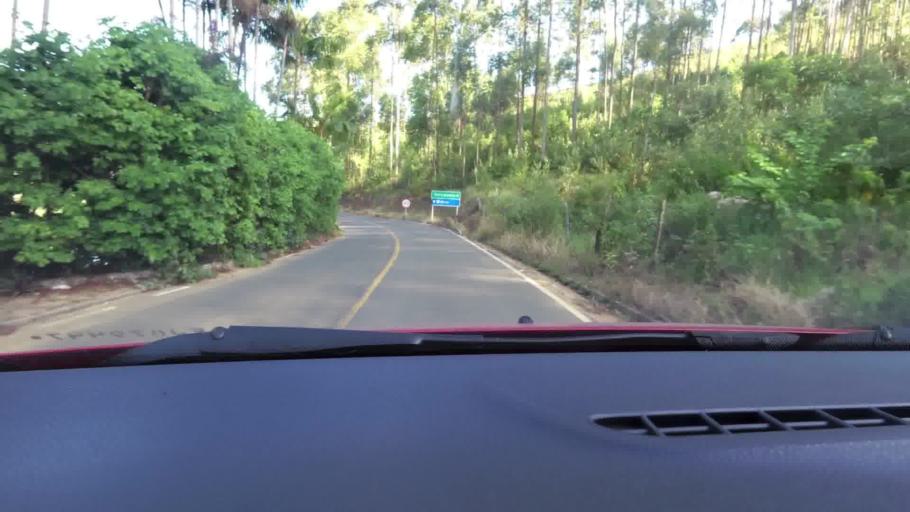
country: BR
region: Espirito Santo
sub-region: Guarapari
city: Guarapari
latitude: -20.5584
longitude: -40.5537
